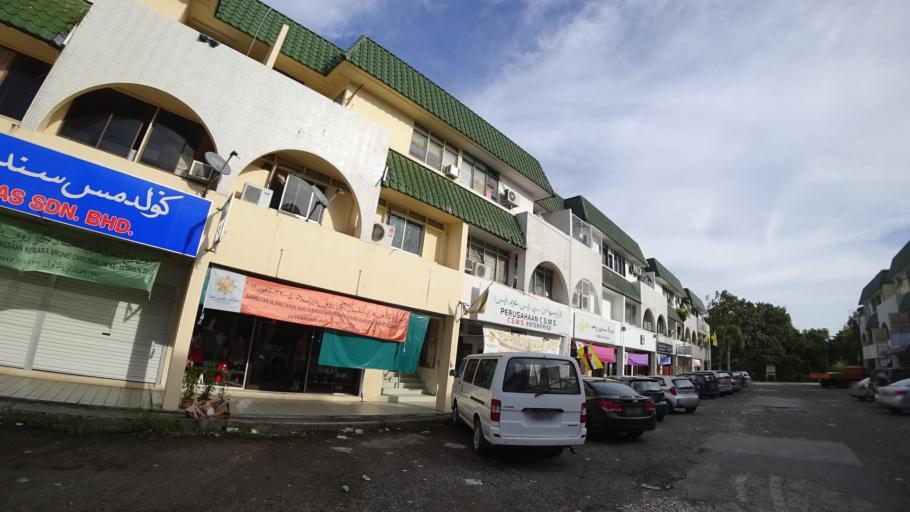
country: BN
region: Brunei and Muara
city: Bandar Seri Begawan
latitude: 4.8782
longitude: 114.8935
